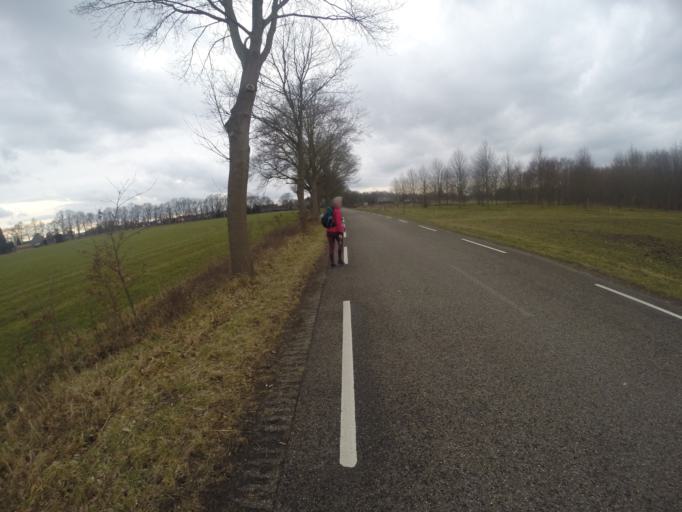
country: NL
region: Gelderland
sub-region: Gemeente Bronckhorst
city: Hengelo
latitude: 52.0487
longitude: 6.3239
